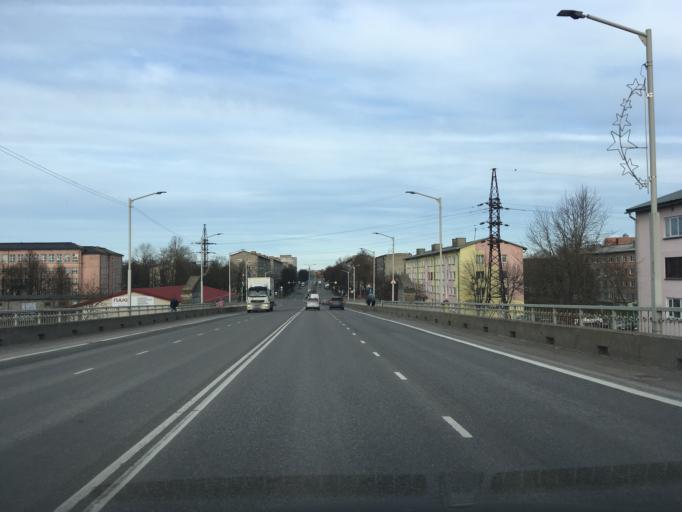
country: EE
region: Ida-Virumaa
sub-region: Narva linn
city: Narva
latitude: 59.3726
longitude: 28.1834
